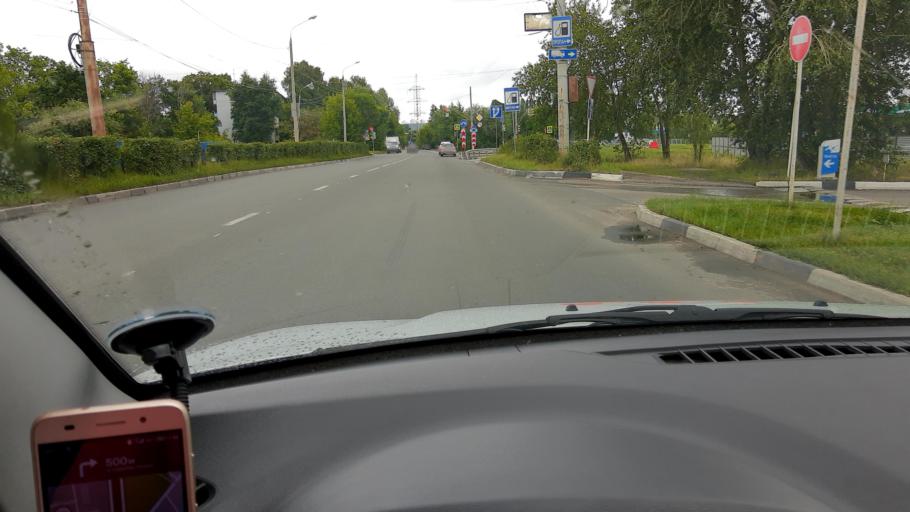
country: RU
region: Nizjnij Novgorod
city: Nizhniy Novgorod
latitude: 56.2545
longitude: 43.9277
